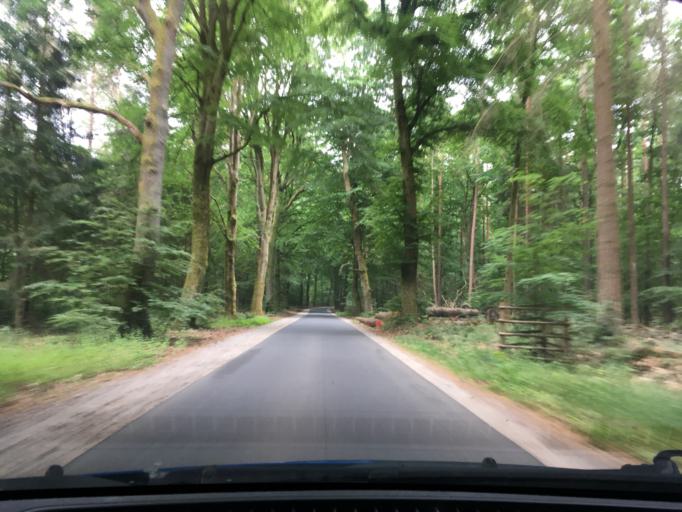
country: DE
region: Lower Saxony
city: Gohrde
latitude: 53.1122
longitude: 10.8803
